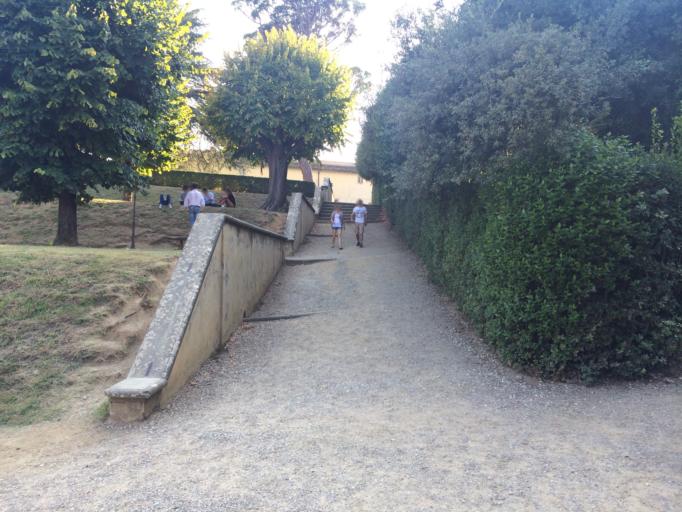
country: IT
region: Tuscany
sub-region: Province of Florence
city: Florence
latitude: 43.7630
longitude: 11.2515
